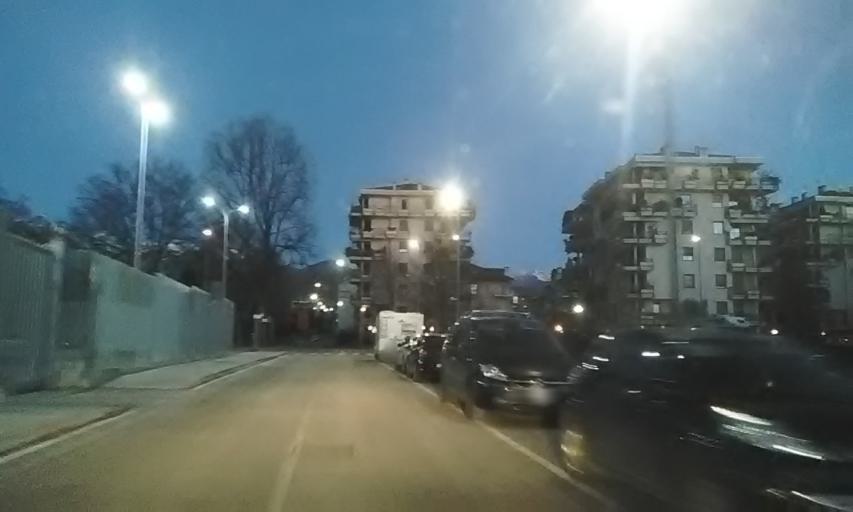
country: IT
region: Piedmont
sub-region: Provincia di Biella
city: Biella
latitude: 45.5564
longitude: 8.0584
